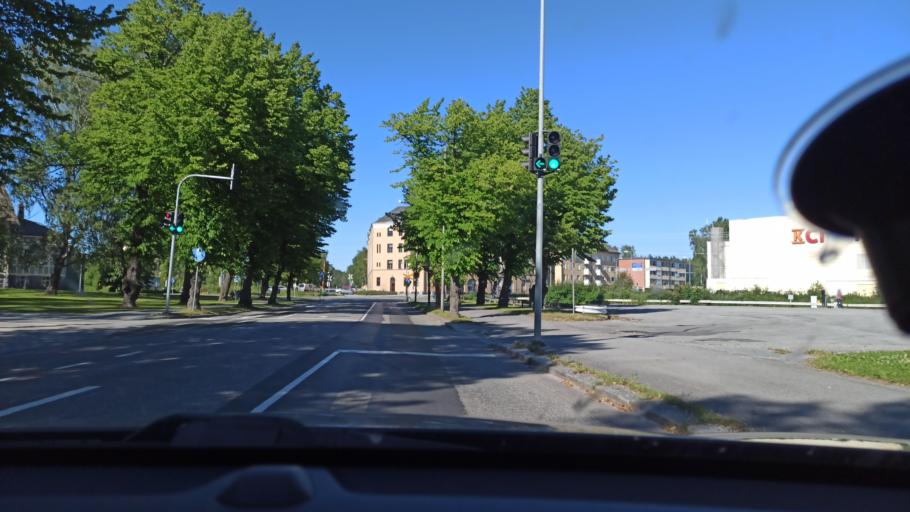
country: FI
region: Ostrobothnia
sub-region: Jakobstadsregionen
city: Jakobstad
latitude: 63.6771
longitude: 22.7111
